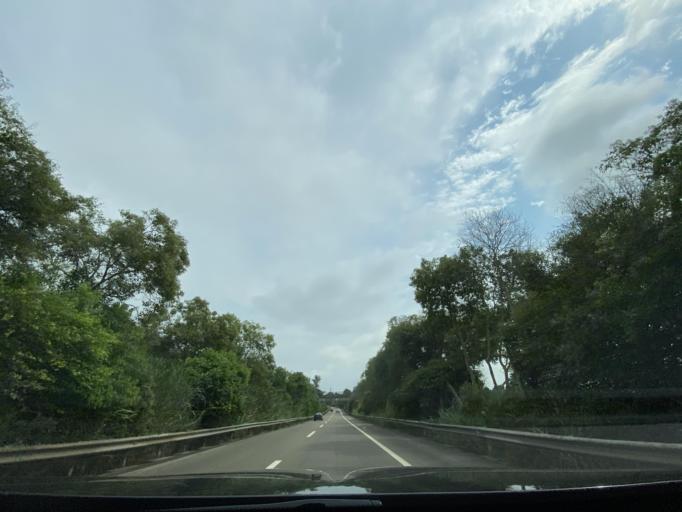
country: CN
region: Sichuan
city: Chonglong
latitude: 29.7072
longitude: 104.9407
